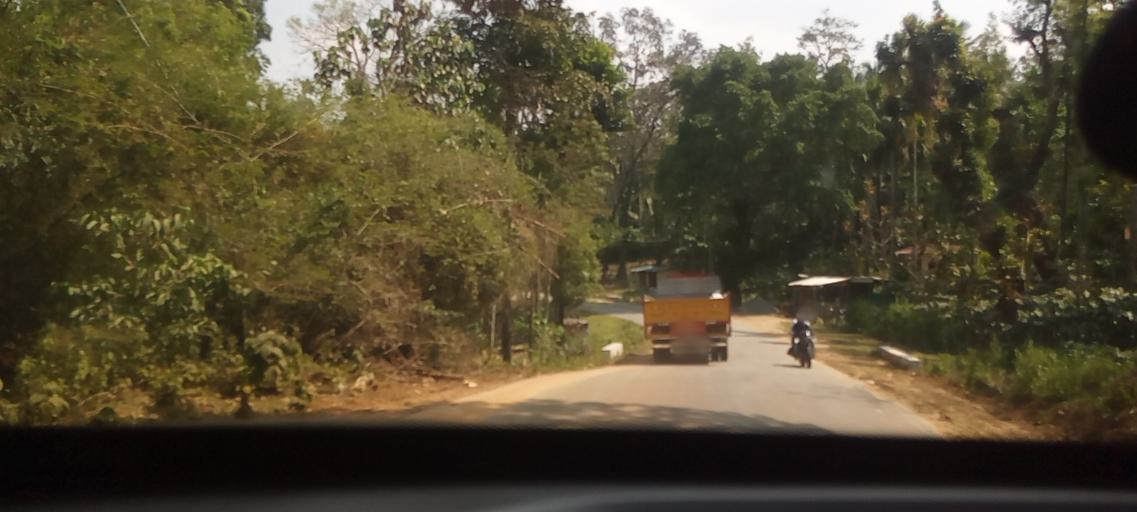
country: IN
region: Karnataka
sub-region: Chikmagalur
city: Mudigere
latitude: 13.3236
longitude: 75.5632
